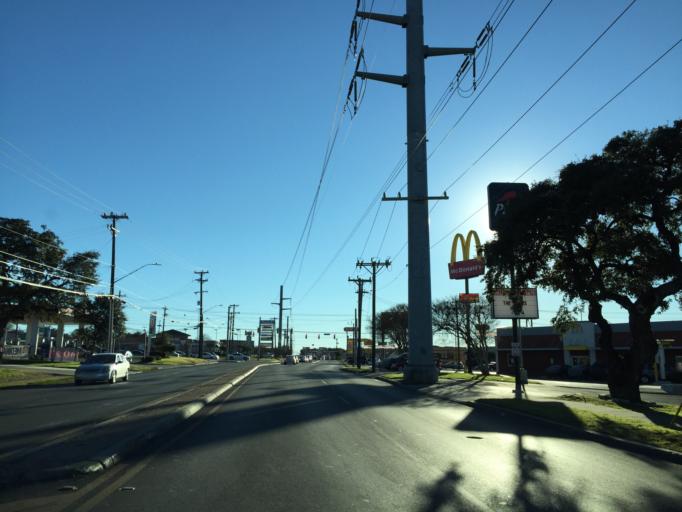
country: US
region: Texas
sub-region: Bexar County
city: Castle Hills
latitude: 29.5473
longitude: -98.5079
